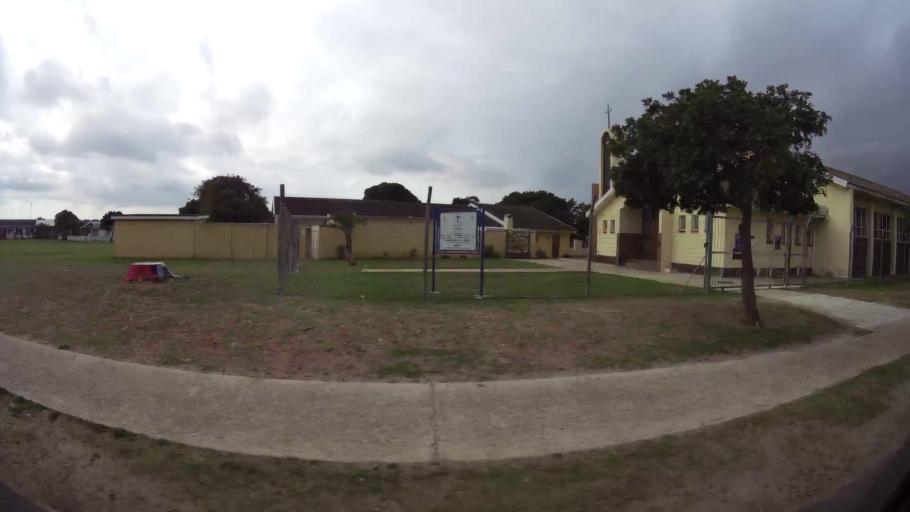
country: ZA
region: Eastern Cape
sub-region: Nelson Mandela Bay Metropolitan Municipality
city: Port Elizabeth
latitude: -33.8961
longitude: 25.5645
